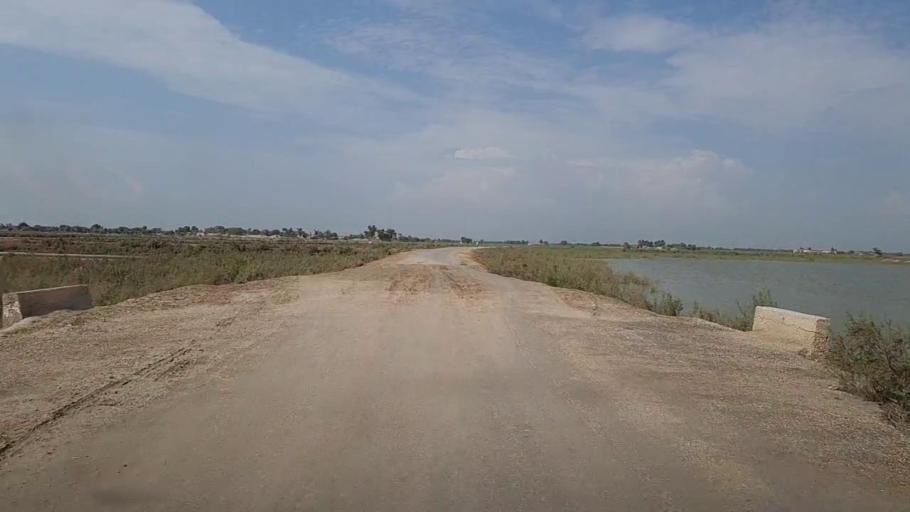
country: PK
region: Sindh
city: Thul
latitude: 28.2859
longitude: 68.8233
